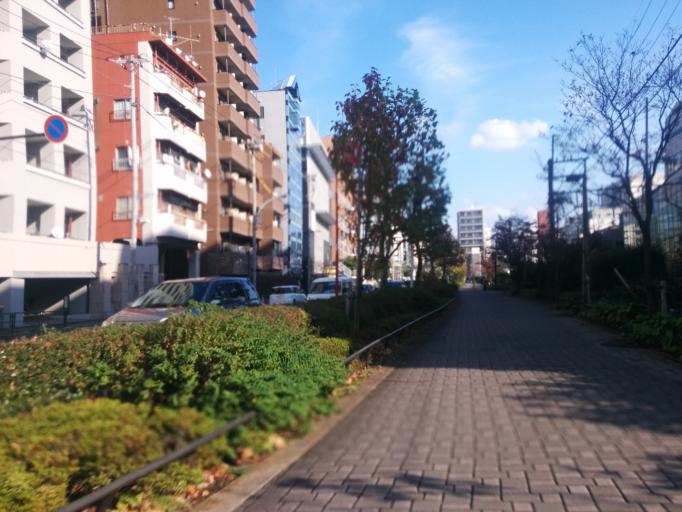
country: JP
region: Tokyo
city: Tokyo
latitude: 35.7163
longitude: 139.7010
